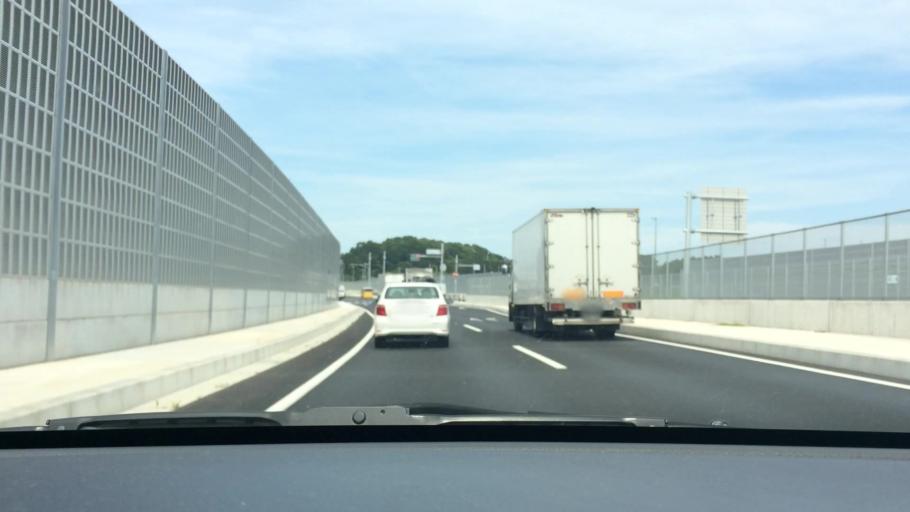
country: JP
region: Chiba
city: Matsudo
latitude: 35.7561
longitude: 139.9156
